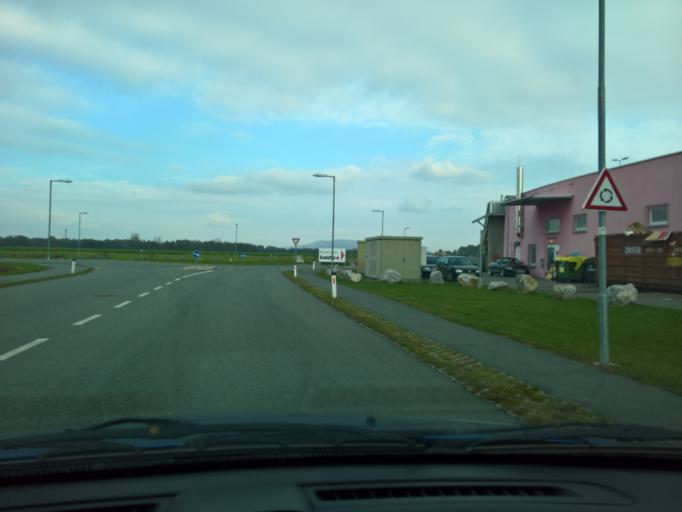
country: AT
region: Styria
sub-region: Politischer Bezirk Leibnitz
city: Kaindorf an der Sulm
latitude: 46.7951
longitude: 15.5535
